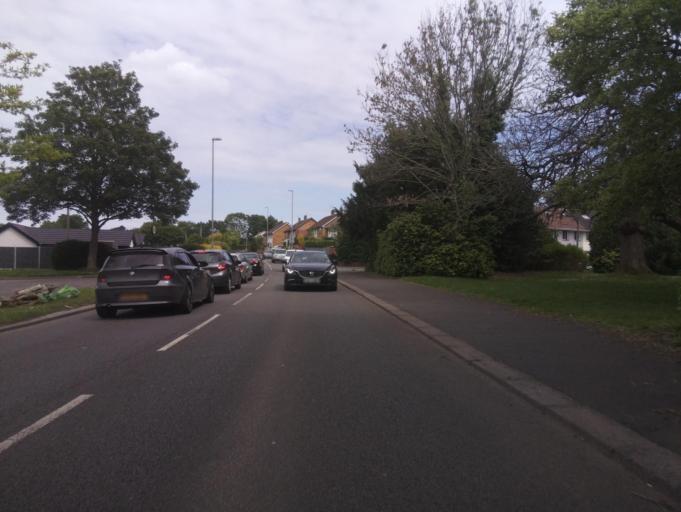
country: GB
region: England
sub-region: Bristol
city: Bristol
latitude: 51.4948
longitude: -2.6247
